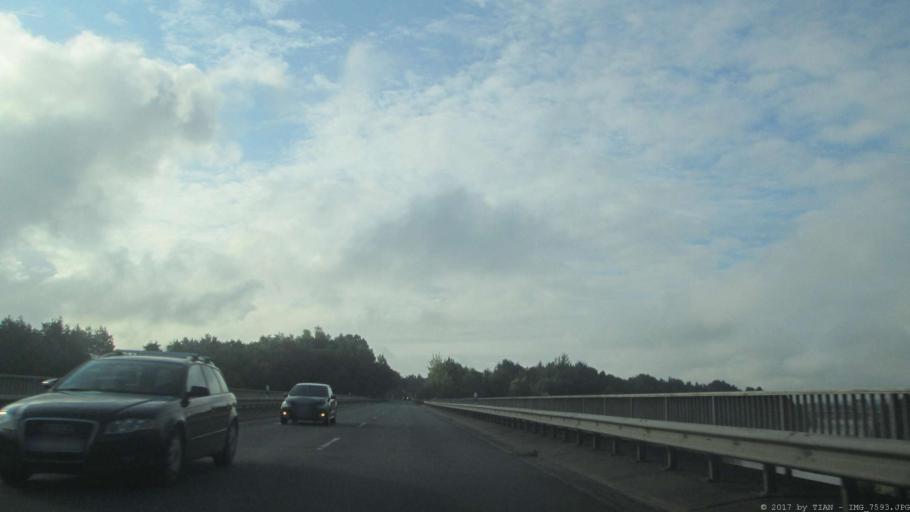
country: DE
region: Lower Saxony
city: Wrestedt
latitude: 52.9267
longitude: 10.6055
